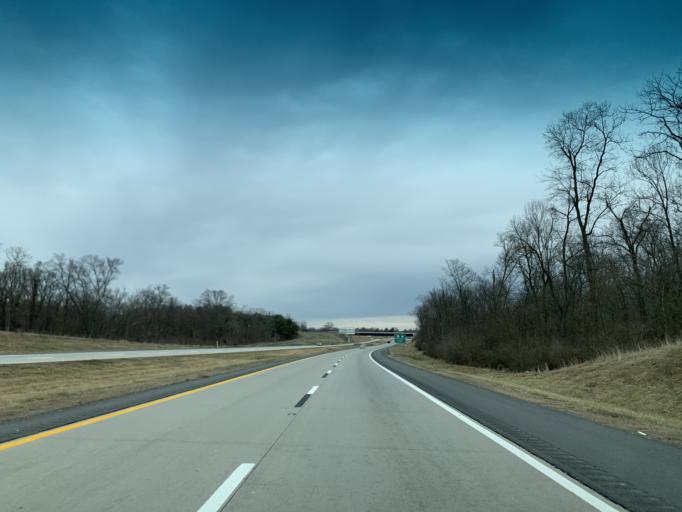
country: US
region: West Virginia
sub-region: Berkeley County
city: Martinsburg
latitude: 39.3938
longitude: -77.9058
